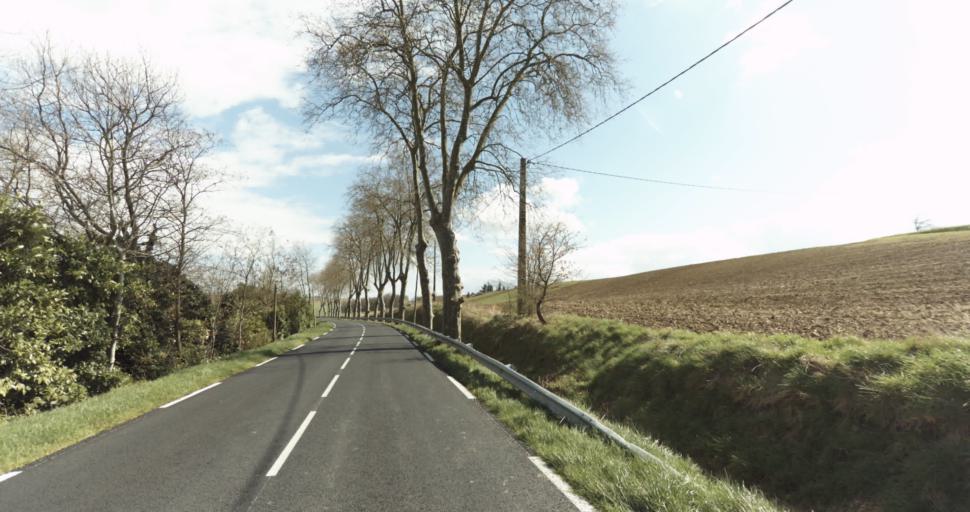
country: FR
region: Midi-Pyrenees
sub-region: Departement de la Haute-Garonne
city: Auterive
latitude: 43.3587
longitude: 1.4995
